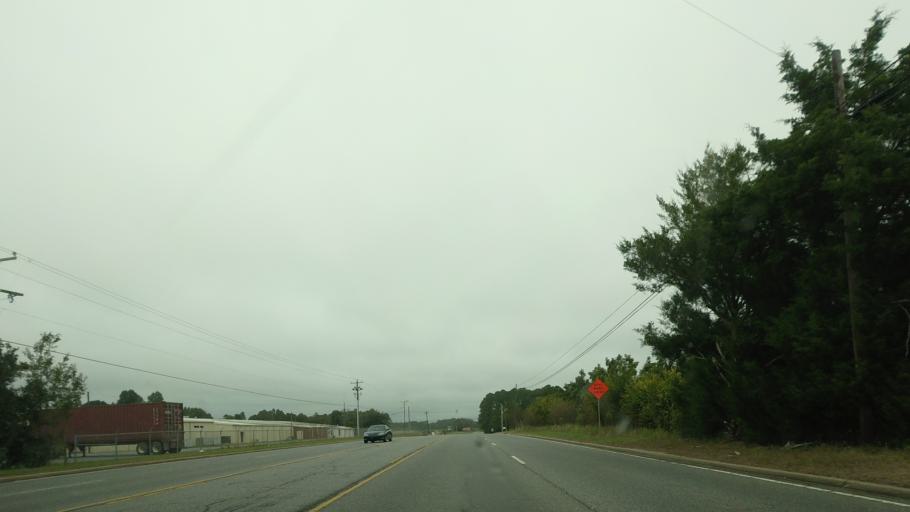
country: US
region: Georgia
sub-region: Irwin County
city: Ocilla
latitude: 31.6269
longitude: -83.2496
